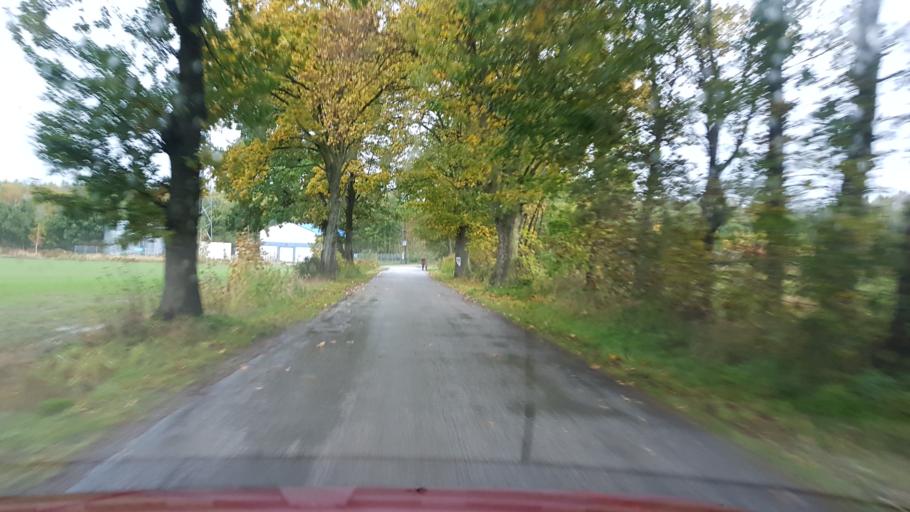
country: PL
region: West Pomeranian Voivodeship
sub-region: Koszalin
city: Koszalin
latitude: 54.1420
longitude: 16.1559
